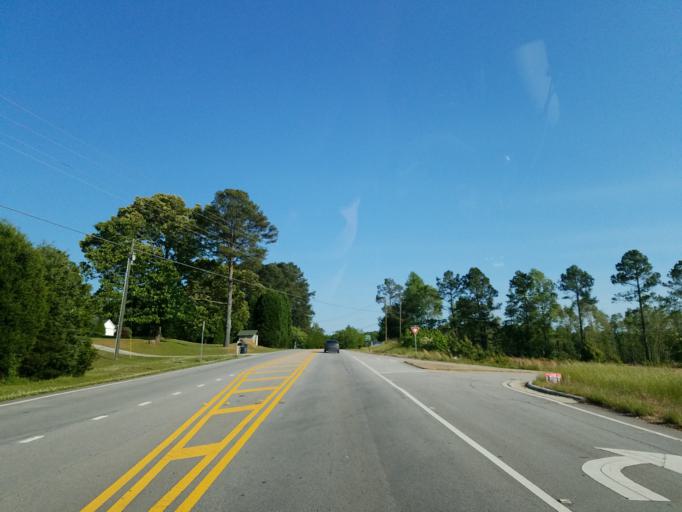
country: US
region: Georgia
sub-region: Carroll County
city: Villa Rica
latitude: 33.7797
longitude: -84.9654
